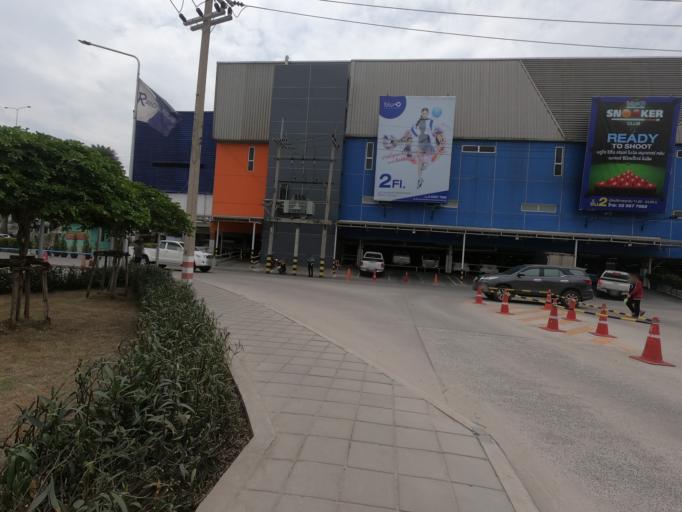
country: TH
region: Bangkok
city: Sai Mai
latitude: 13.9260
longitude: 100.6548
